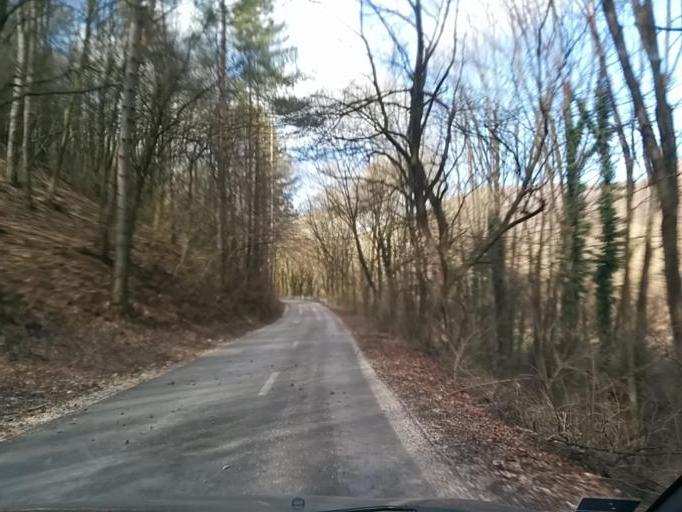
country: SK
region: Nitriansky
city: Cachtice
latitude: 48.7337
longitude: 17.7759
